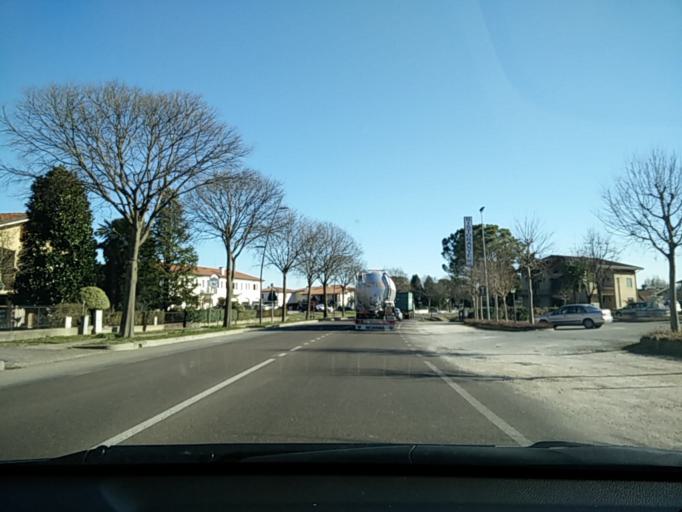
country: IT
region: Veneto
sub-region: Provincia di Treviso
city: Portobuffole
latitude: 45.8578
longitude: 12.5375
